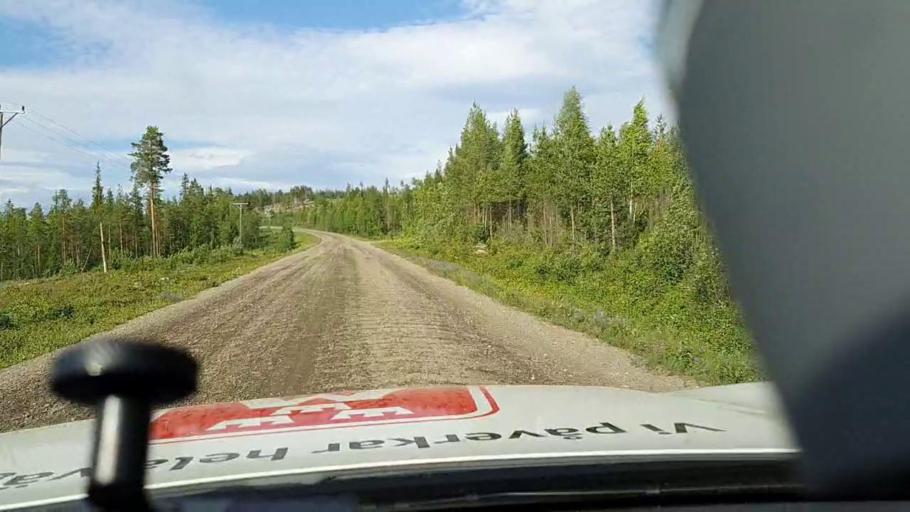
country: SE
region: Norrbotten
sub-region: Alvsbyns Kommun
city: AElvsbyn
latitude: 66.1636
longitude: 21.0531
